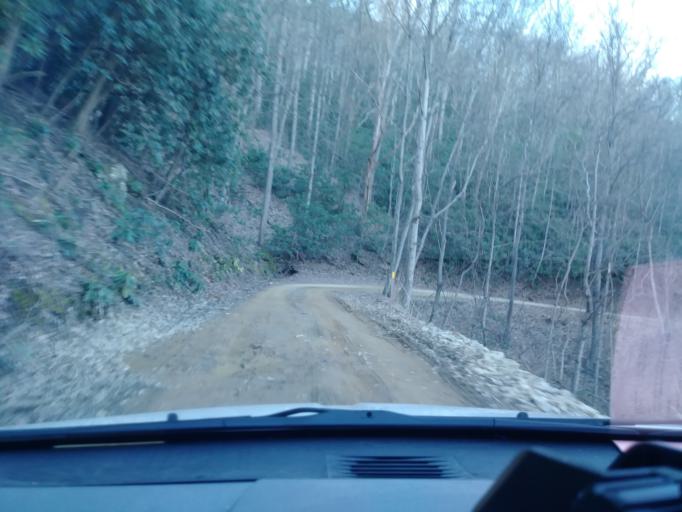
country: US
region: Tennessee
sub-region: Greene County
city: Tusculum
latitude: 36.0746
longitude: -82.6870
